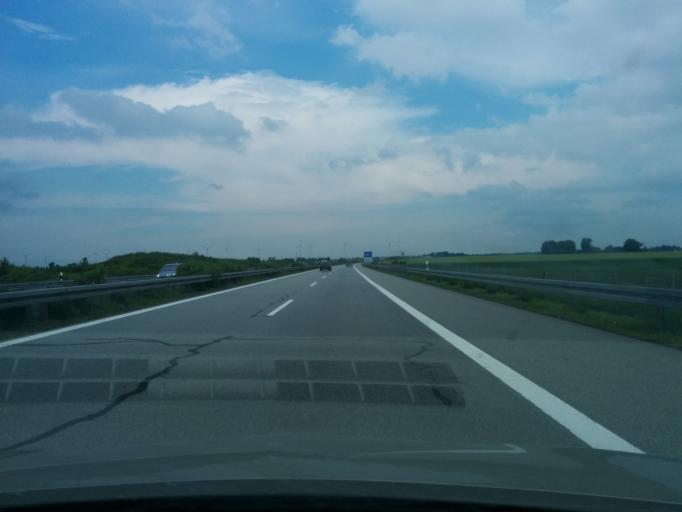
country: DE
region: Mecklenburg-Vorpommern
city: Jarmen
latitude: 53.8483
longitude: 13.3317
